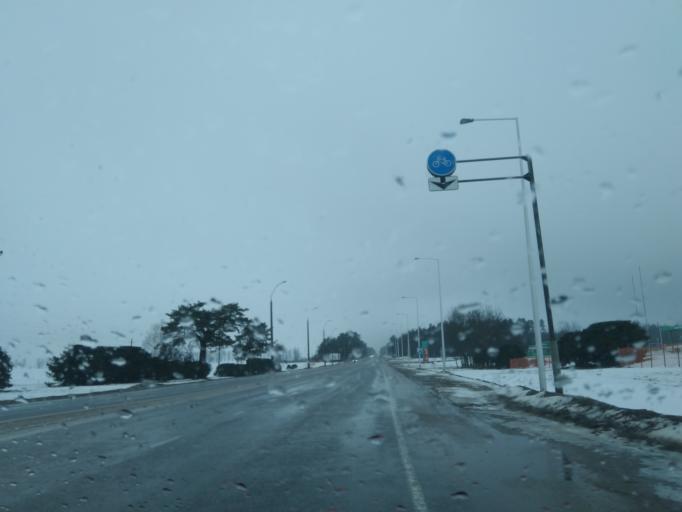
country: BY
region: Minsk
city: Nyasvizh
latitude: 53.2392
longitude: 26.6331
